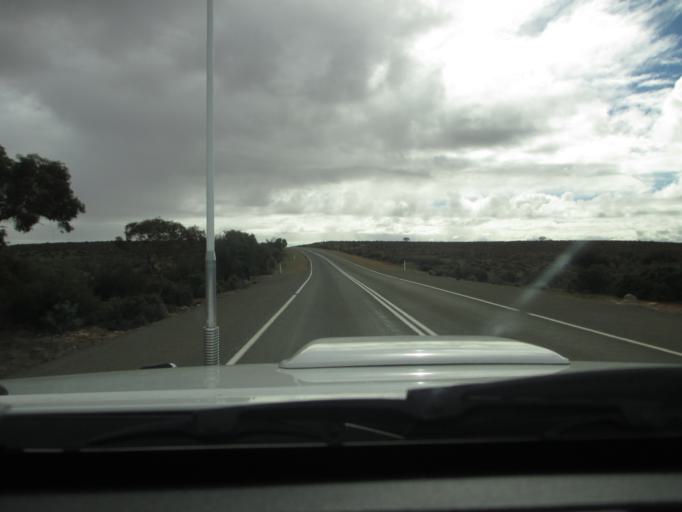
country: AU
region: South Australia
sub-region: Flinders Ranges
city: Quorn
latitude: -31.5614
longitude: 138.4288
